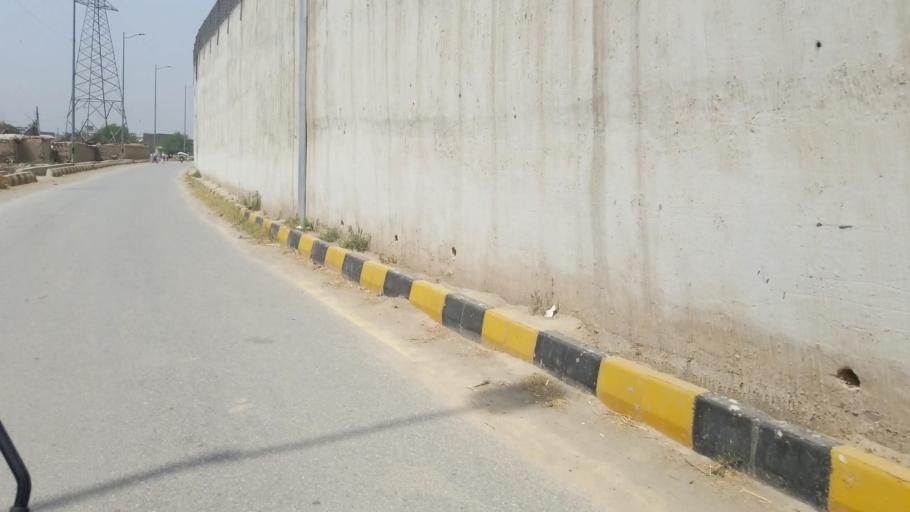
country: PK
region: Khyber Pakhtunkhwa
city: Peshawar
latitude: 34.0297
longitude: 71.5483
